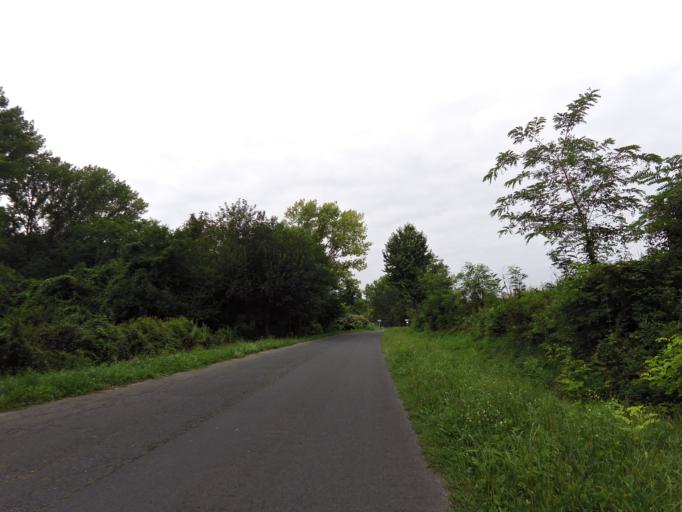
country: HU
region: Zala
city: Vonyarcvashegy
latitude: 46.8423
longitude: 17.3545
